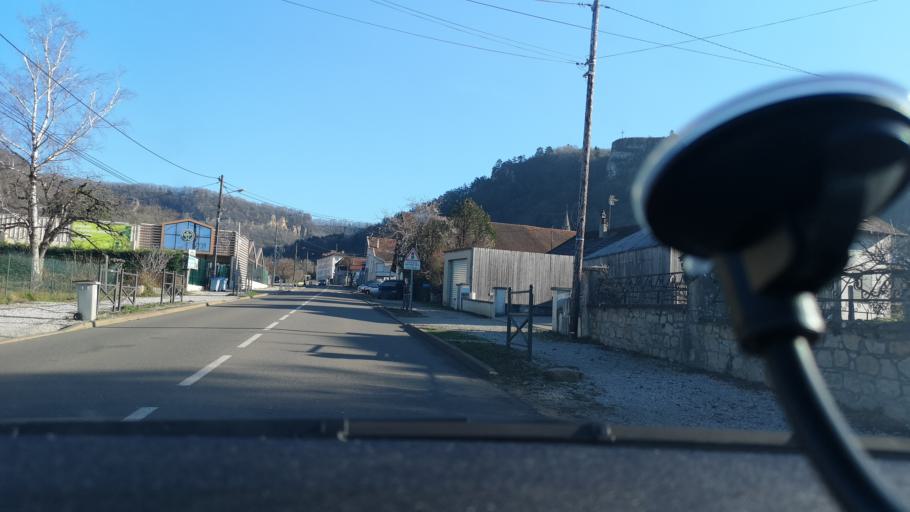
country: FR
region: Franche-Comte
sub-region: Departement du Jura
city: Poligny
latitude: 46.8340
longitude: 5.7007
